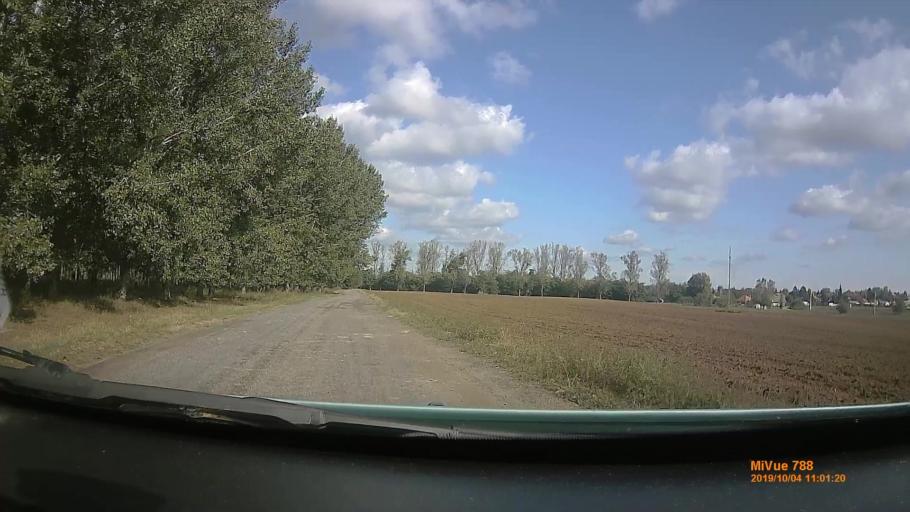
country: HU
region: Szabolcs-Szatmar-Bereg
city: Nyirtelek
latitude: 47.9829
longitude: 21.6716
